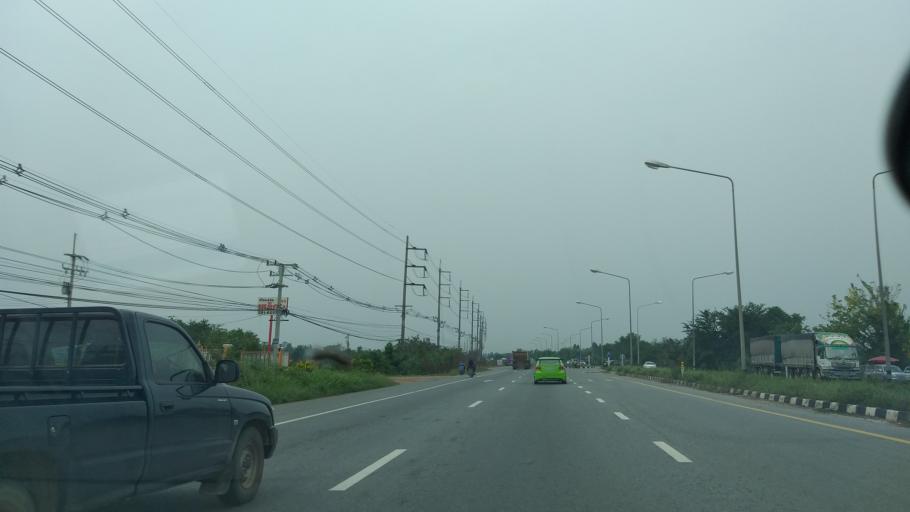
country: TH
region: Chon Buri
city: Ko Chan
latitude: 13.3965
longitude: 101.2809
